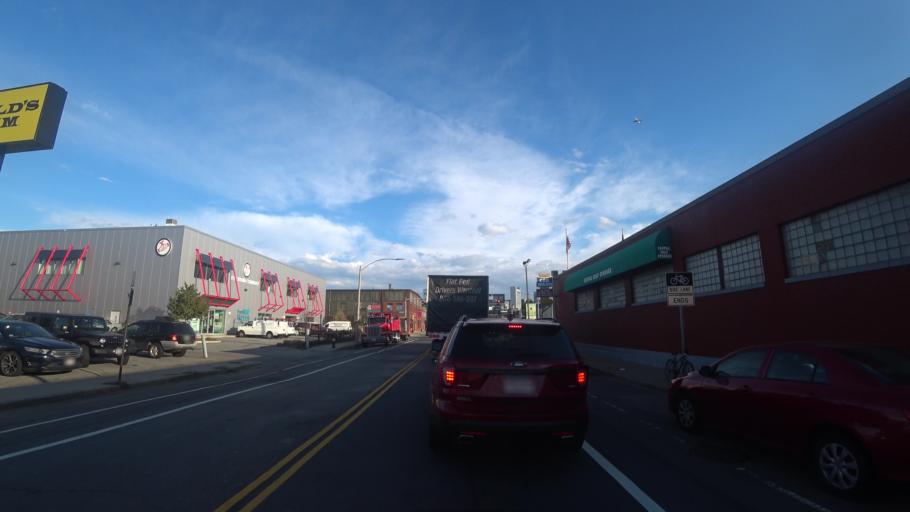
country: US
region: Massachusetts
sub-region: Suffolk County
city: South Boston
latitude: 42.3368
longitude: -71.0571
